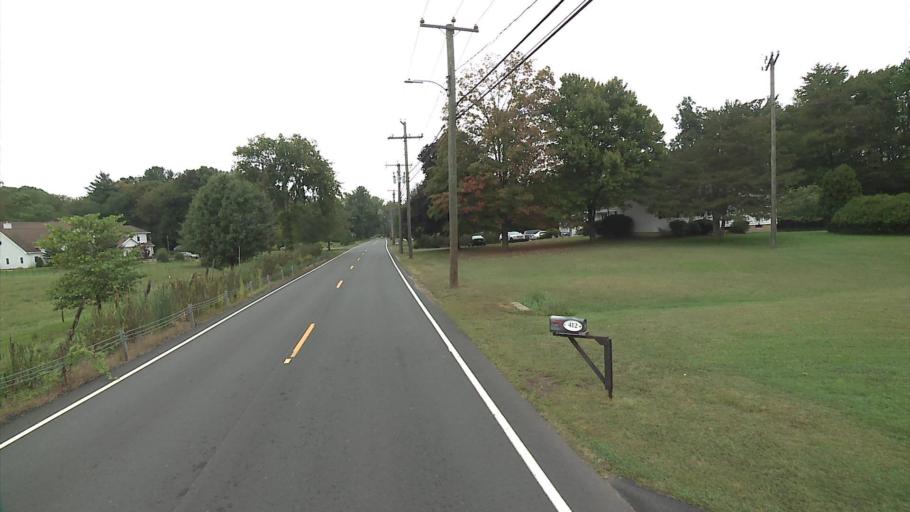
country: US
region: Connecticut
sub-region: Hartford County
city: Windsor
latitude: 41.8637
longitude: -72.6547
